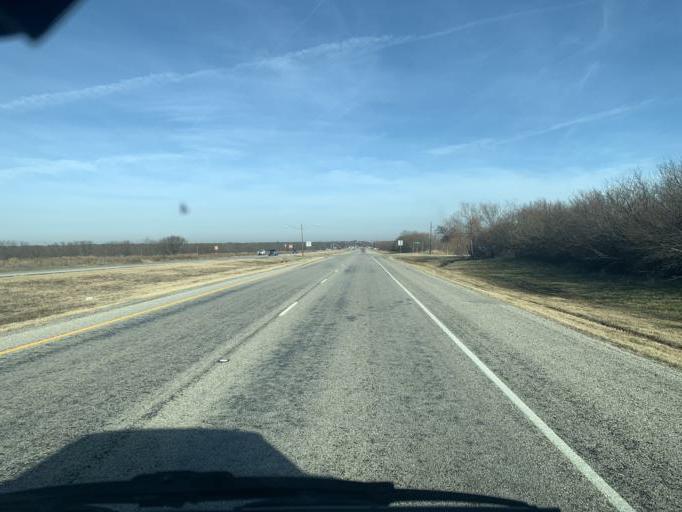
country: US
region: Texas
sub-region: Dallas County
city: Cedar Hill
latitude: 32.6503
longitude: -96.9766
